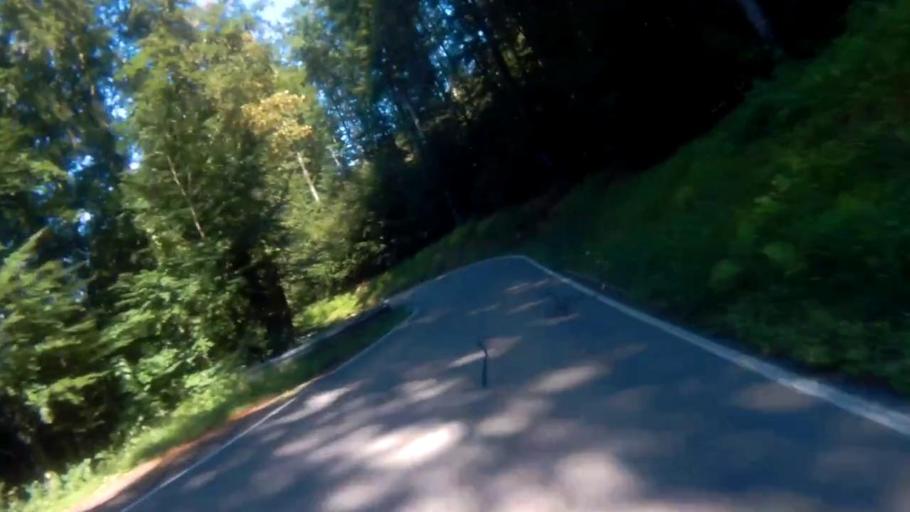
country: DE
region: Baden-Wuerttemberg
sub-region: Freiburg Region
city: Hausen
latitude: 47.6819
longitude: 7.8226
